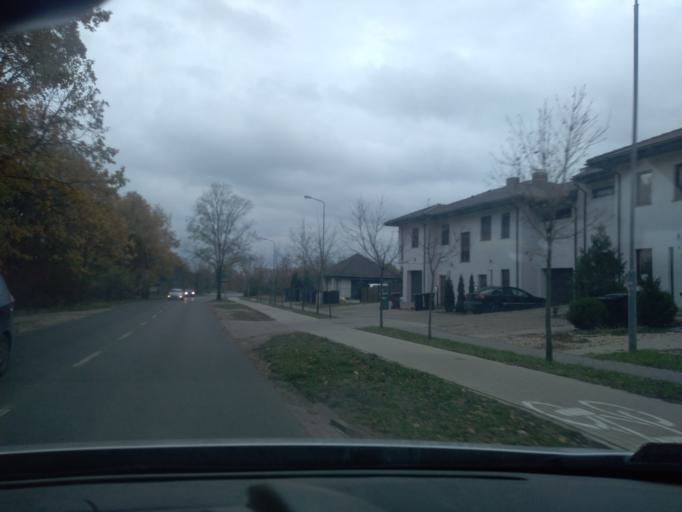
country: PL
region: Greater Poland Voivodeship
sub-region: Powiat poznanski
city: Suchy Las
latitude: 52.4724
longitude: 16.9000
